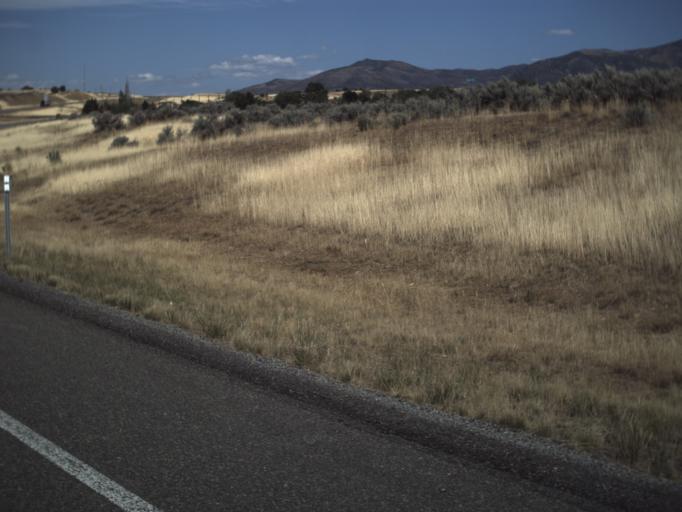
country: US
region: Utah
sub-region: Millard County
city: Fillmore
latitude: 39.0843
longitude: -112.2744
